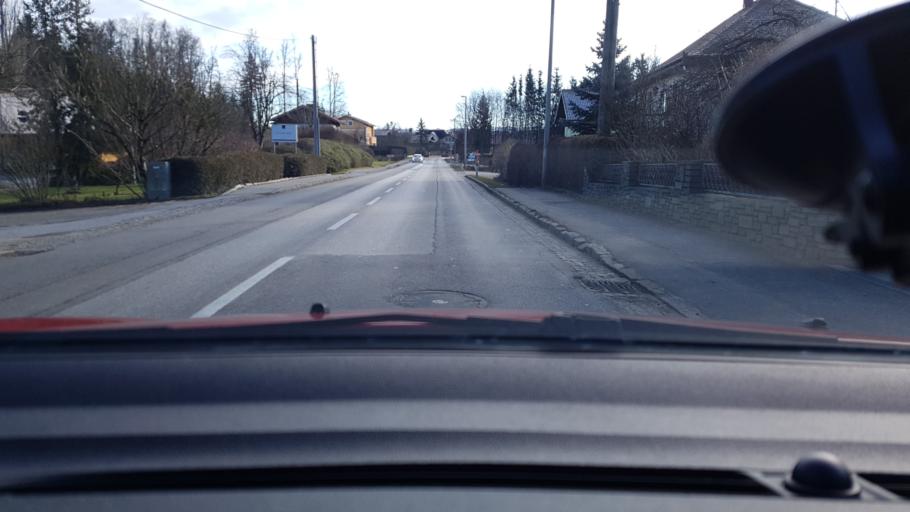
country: AT
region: Salzburg
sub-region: Politischer Bezirk Salzburg-Umgebung
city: Dorfbeuern
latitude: 48.0501
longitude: 12.9863
